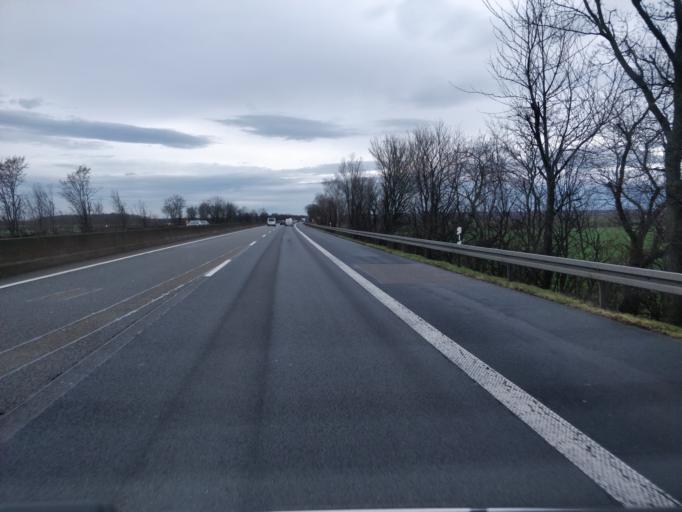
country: DE
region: North Rhine-Westphalia
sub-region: Regierungsbezirk Koln
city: Weilerswist
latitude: 50.7313
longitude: 6.7888
